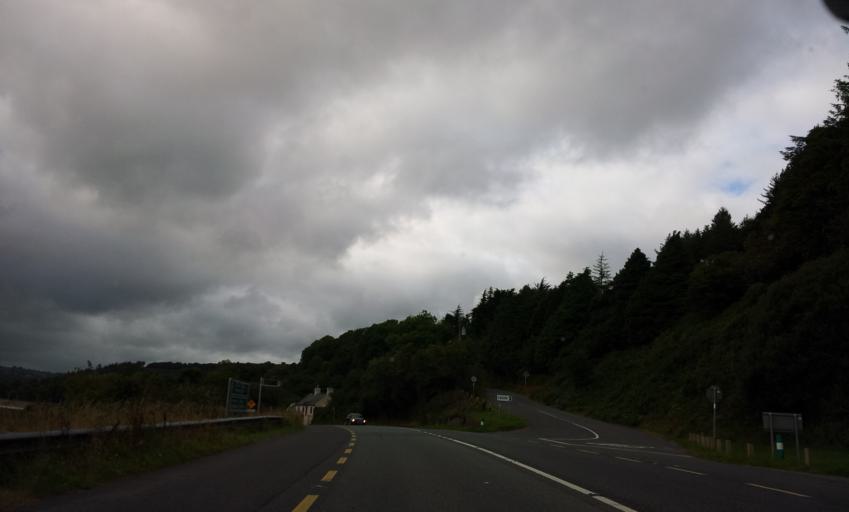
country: IE
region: Munster
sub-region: County Cork
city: Youghal
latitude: 51.9802
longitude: -7.8511
